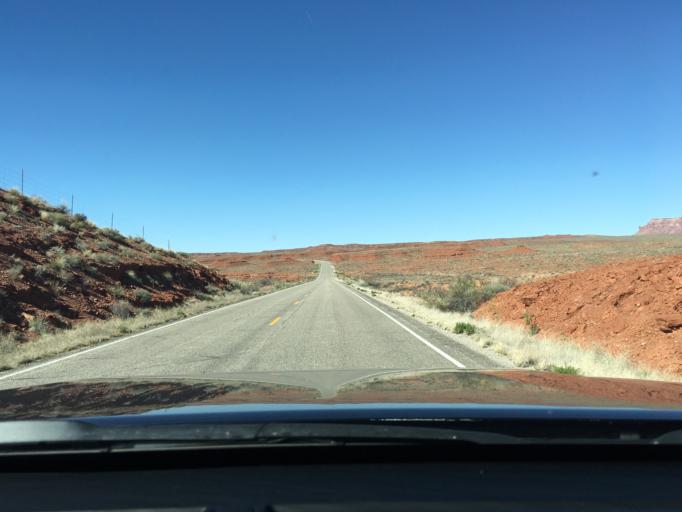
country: US
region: Utah
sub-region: San Juan County
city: Blanding
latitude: 37.2153
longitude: -109.8390
